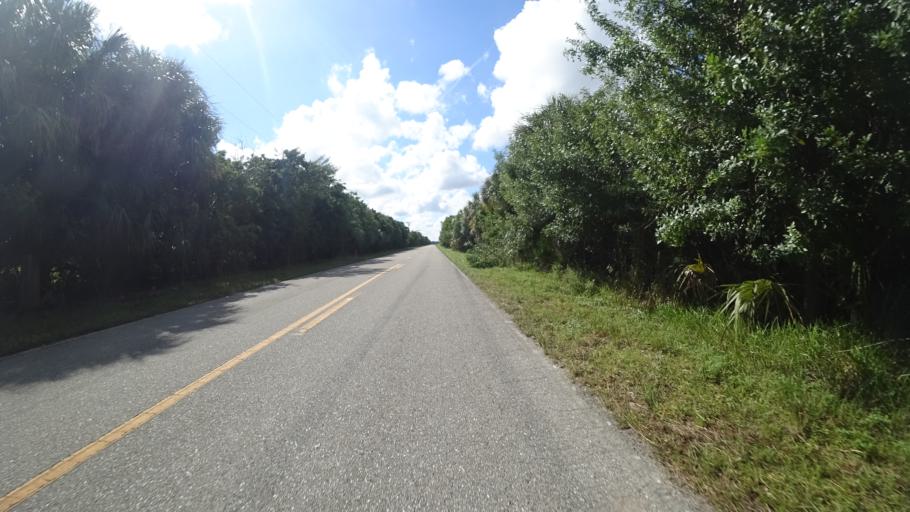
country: US
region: Florida
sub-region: Manatee County
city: Ellenton
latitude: 27.6097
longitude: -82.4817
